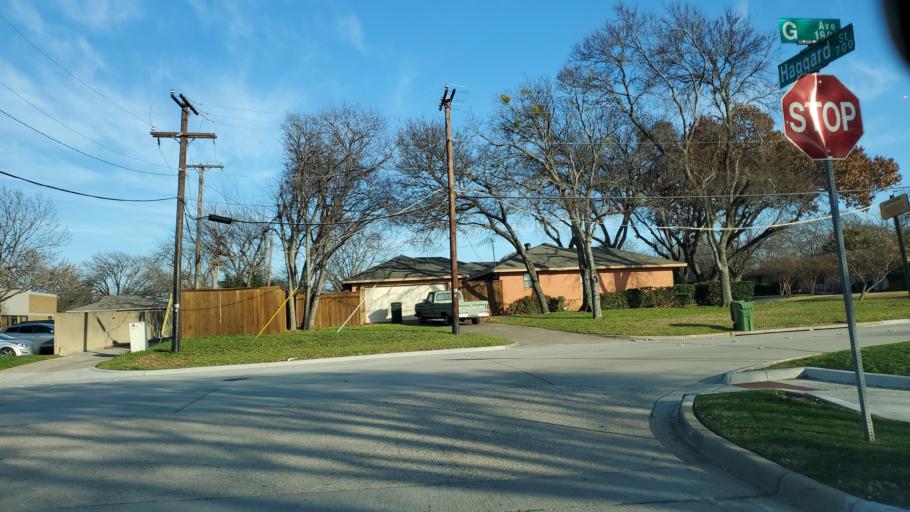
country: US
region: Texas
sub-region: Collin County
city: Plano
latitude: 33.0262
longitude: -96.7051
